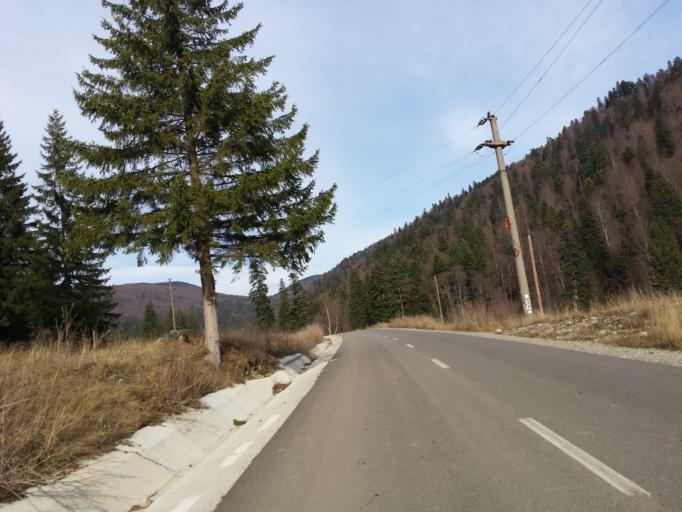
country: RO
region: Prahova
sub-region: Oras Azuga
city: Azuga
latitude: 45.4366
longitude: 25.5293
